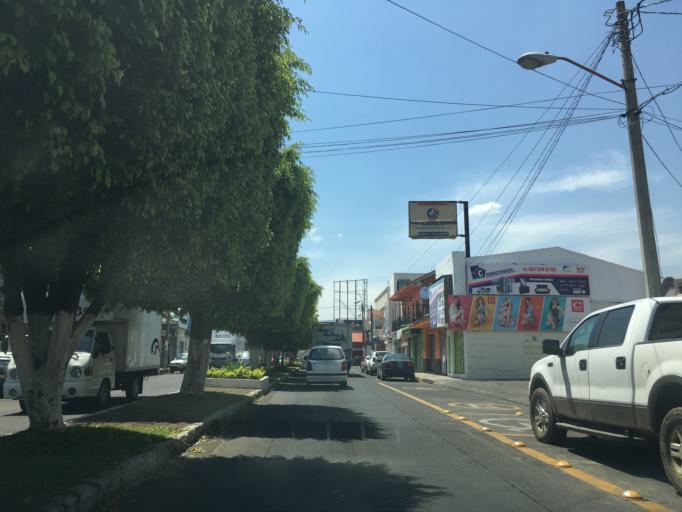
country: MX
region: Michoacan
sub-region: Uruapan
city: Uruapan
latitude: 19.4160
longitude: -102.0556
